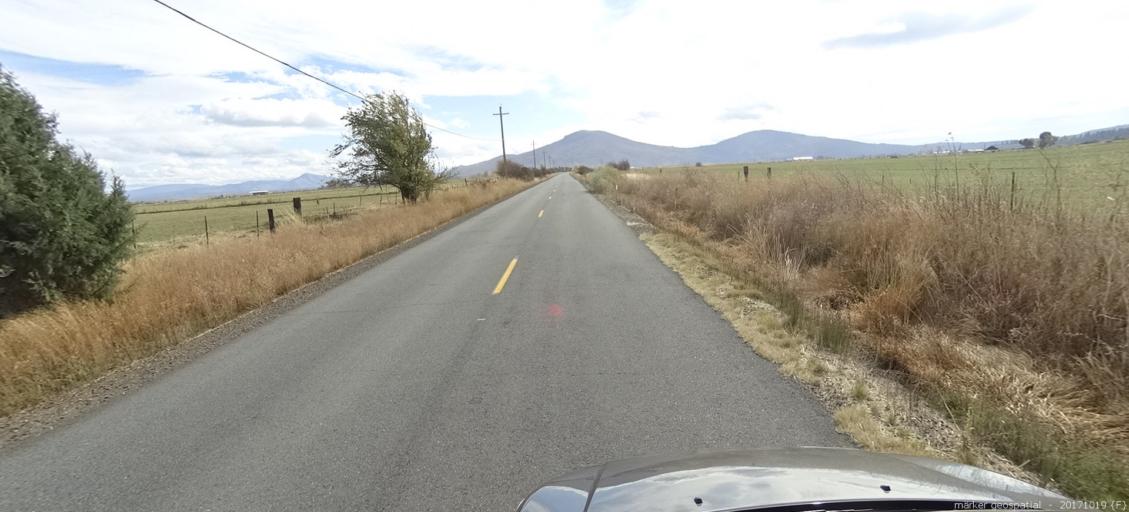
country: US
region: California
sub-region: Shasta County
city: Burney
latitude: 41.0835
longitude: -121.4932
